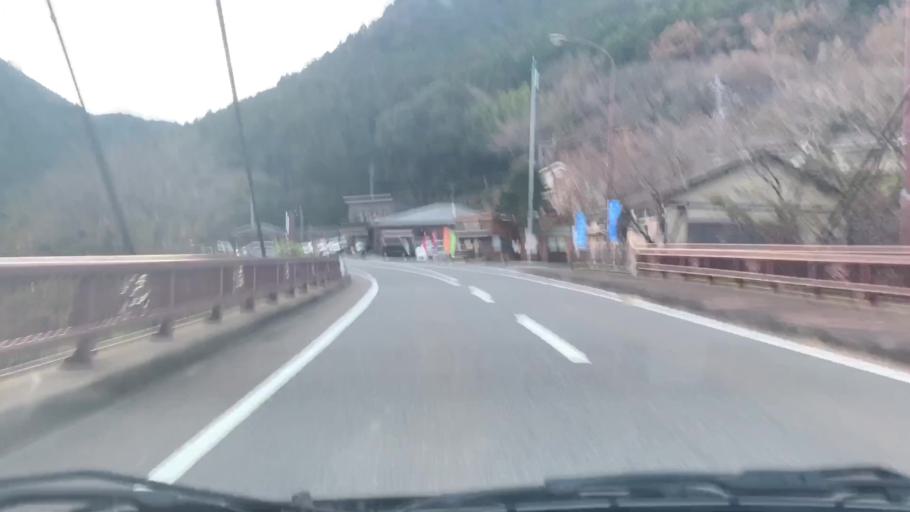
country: JP
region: Nagasaki
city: Omura
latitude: 32.9820
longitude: 130.0251
